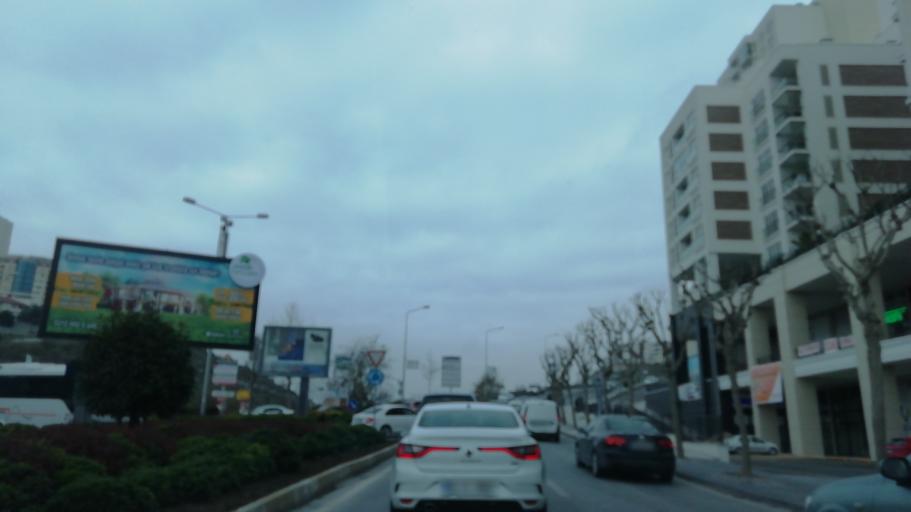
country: TR
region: Istanbul
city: Esenyurt
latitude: 41.0727
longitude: 28.6928
